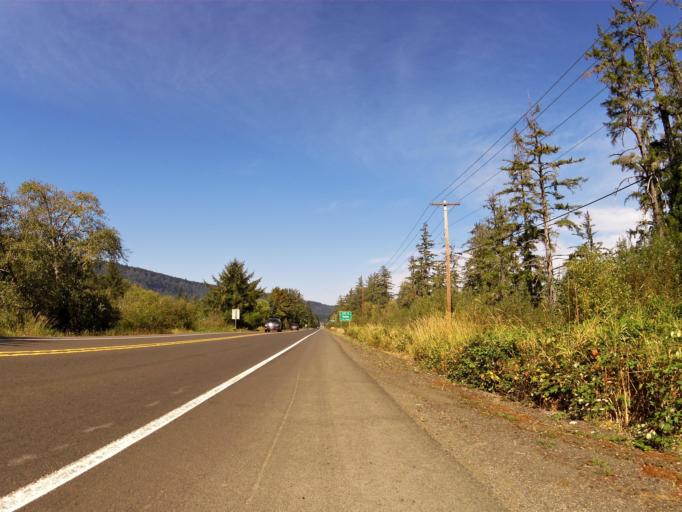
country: US
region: Washington
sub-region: Wahkiakum County
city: Cathlamet
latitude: 46.1371
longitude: -123.3850
